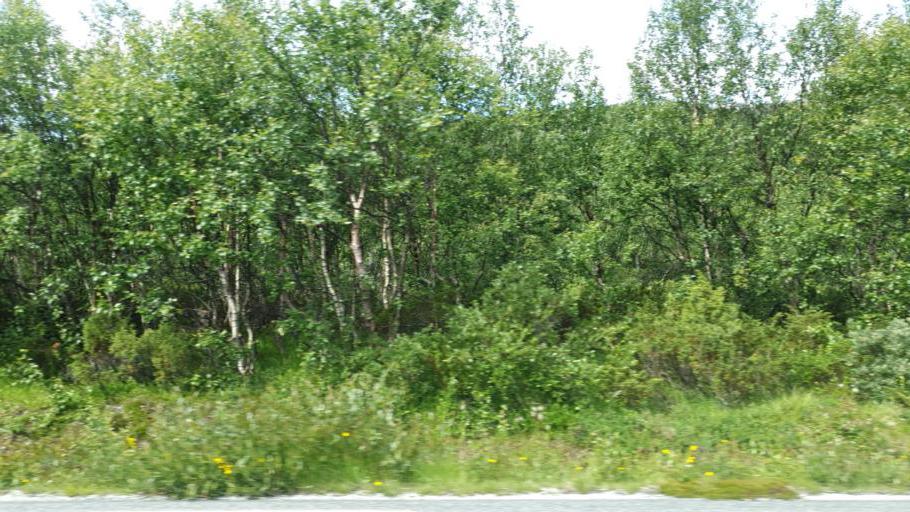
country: NO
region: Oppland
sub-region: Oystre Slidre
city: Heggenes
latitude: 61.4940
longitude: 8.8436
